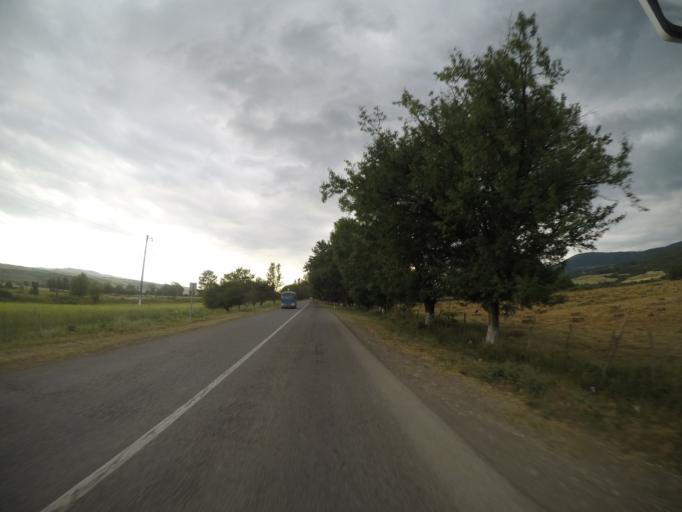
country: AZ
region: Ismayilli
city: Ismayilli
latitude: 40.7514
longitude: 48.2388
